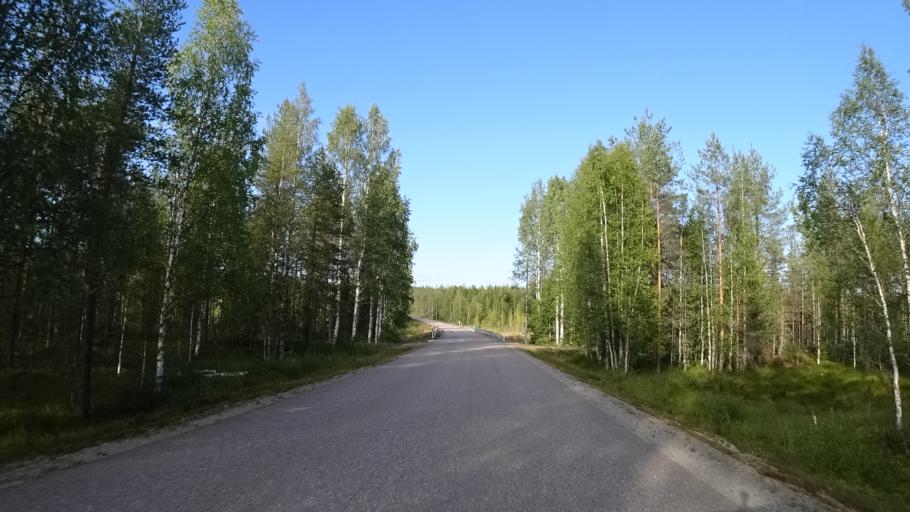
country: FI
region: North Karelia
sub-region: Joensuu
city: Eno
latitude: 63.0289
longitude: 30.5207
